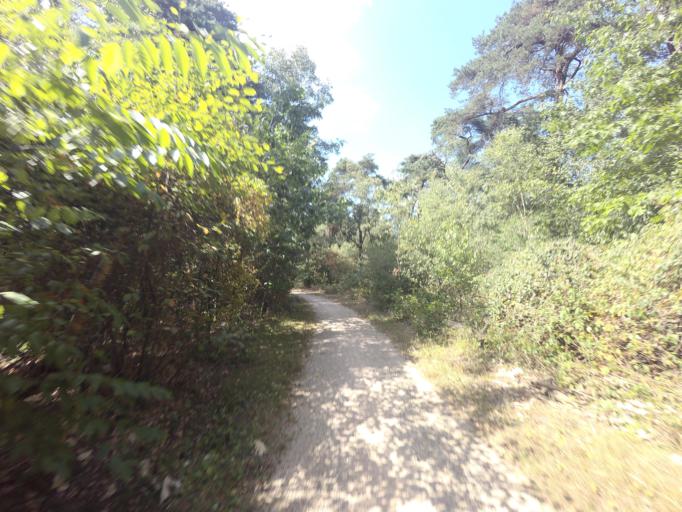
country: NL
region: Utrecht
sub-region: Gemeente Zeist
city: Zeist
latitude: 52.0863
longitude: 5.2677
